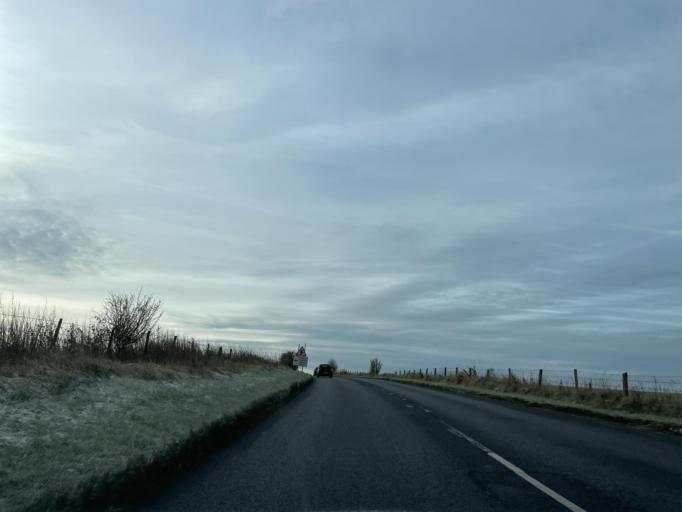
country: GB
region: England
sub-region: Borough of Swindon
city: Wroughton
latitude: 51.5149
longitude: -1.8113
